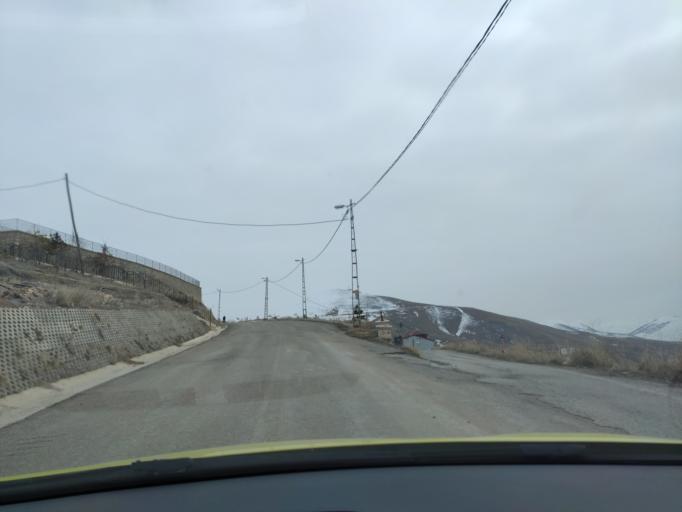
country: TR
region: Bayburt
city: Bayburt
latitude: 40.2599
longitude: 40.2185
